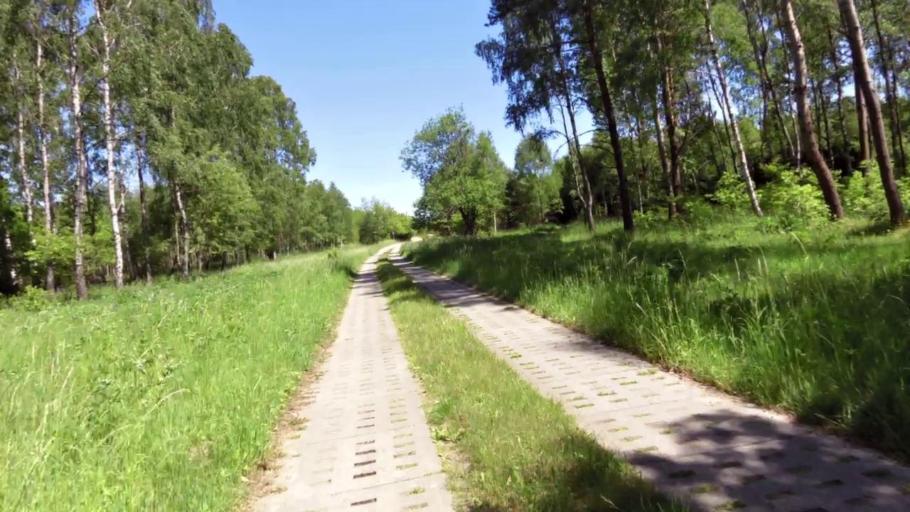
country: PL
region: West Pomeranian Voivodeship
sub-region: Powiat szczecinecki
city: Borne Sulinowo
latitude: 53.5833
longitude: 16.6498
